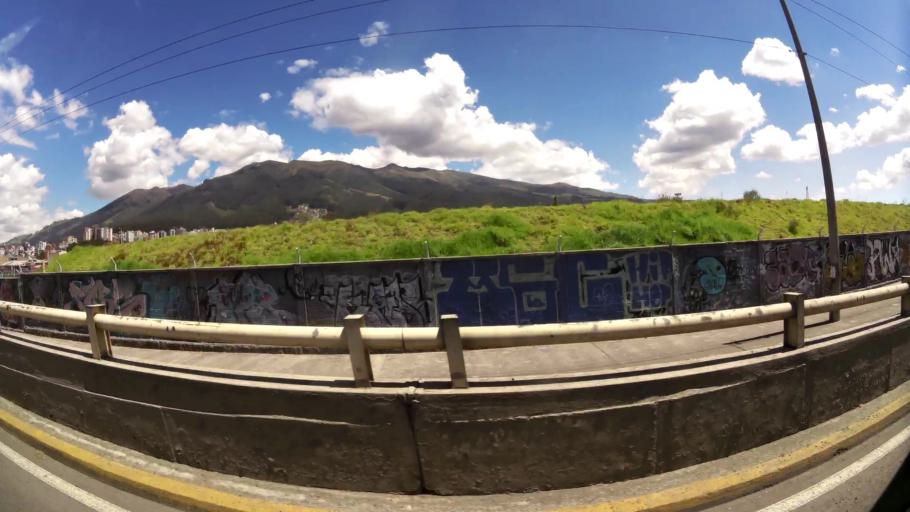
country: EC
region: Pichincha
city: Quito
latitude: -0.1561
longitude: -78.4852
